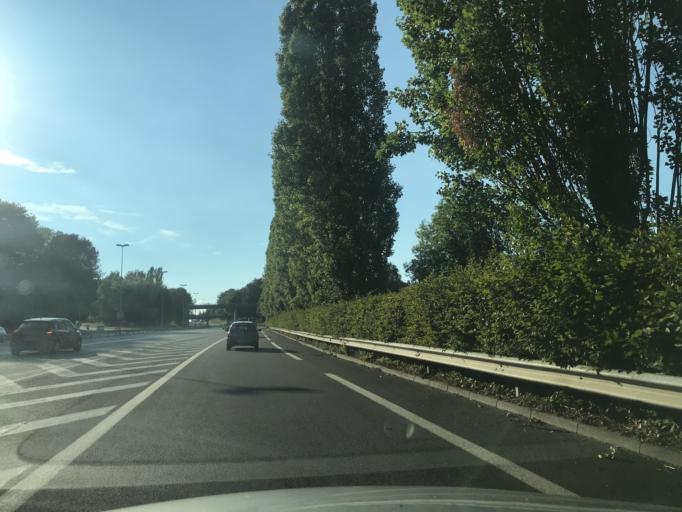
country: FR
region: Rhone-Alpes
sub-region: Departement de la Haute-Savoie
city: Annecy
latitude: 45.8969
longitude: 6.1099
